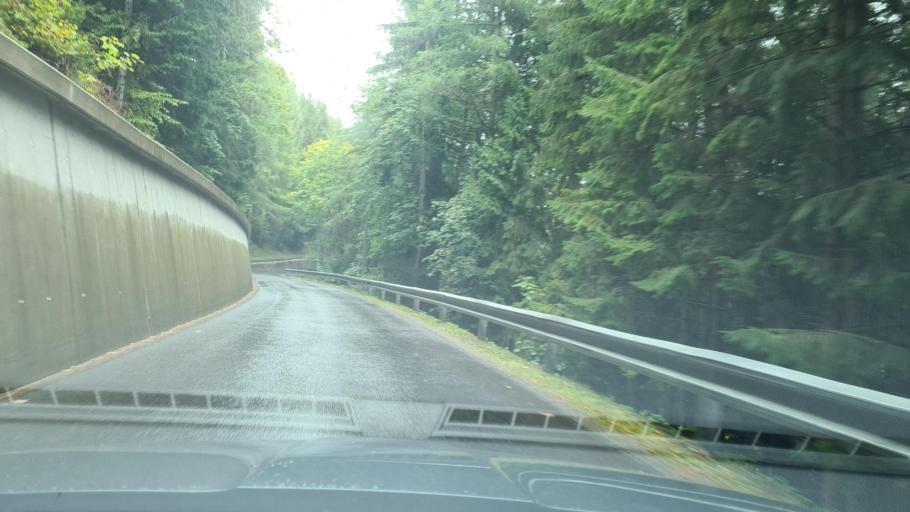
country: AT
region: Styria
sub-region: Politischer Bezirk Weiz
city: Passail
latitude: 47.3321
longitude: 15.4743
